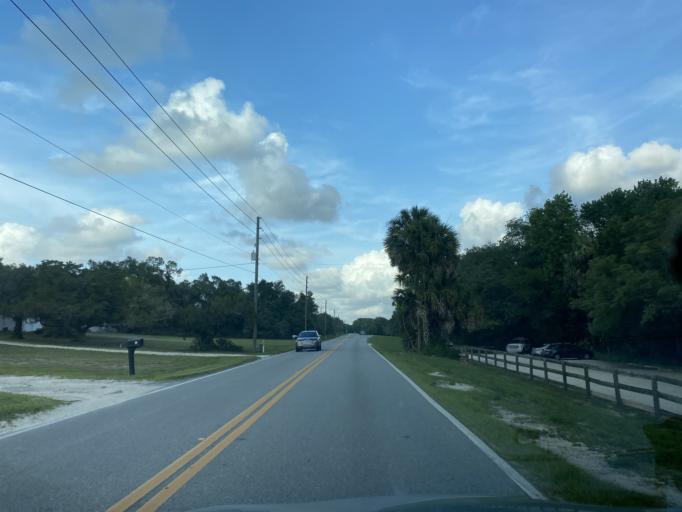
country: US
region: Florida
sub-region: Volusia County
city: DeBary
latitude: 28.8668
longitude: -81.3144
